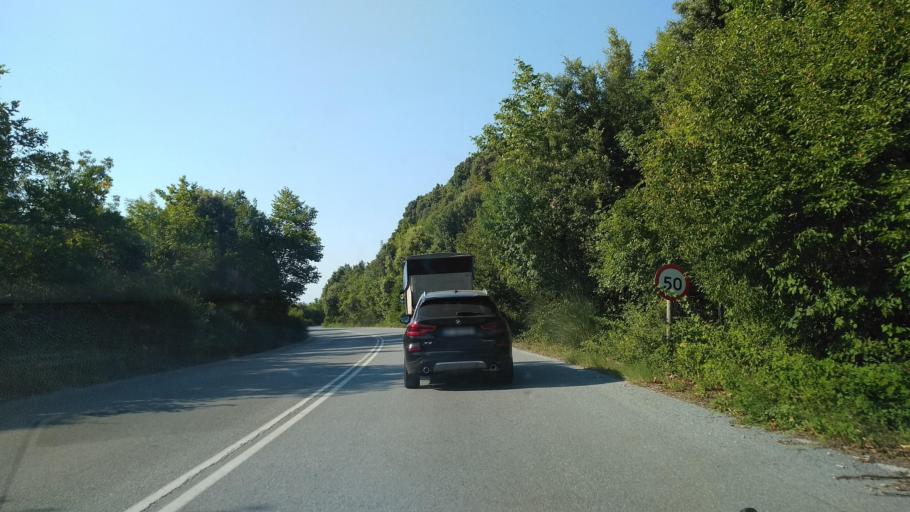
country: GR
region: Central Macedonia
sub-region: Nomos Chalkidikis
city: Stratonion
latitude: 40.5274
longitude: 23.8242
